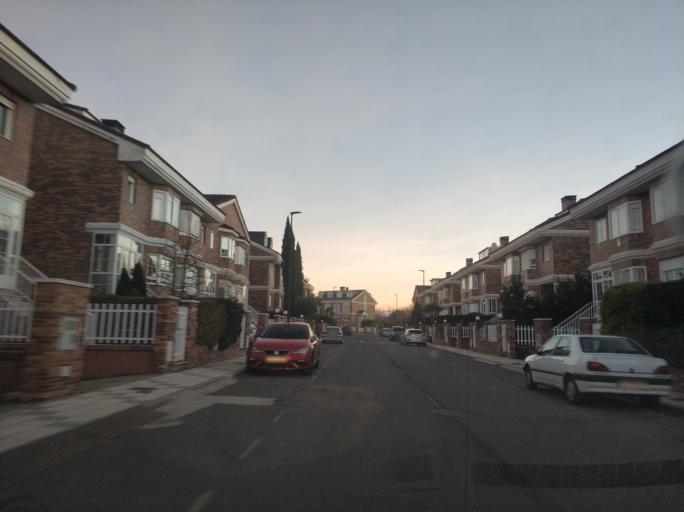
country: ES
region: Castille and Leon
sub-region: Provincia de Salamanca
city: Santa Marta de Tormes
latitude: 40.9531
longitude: -5.6454
